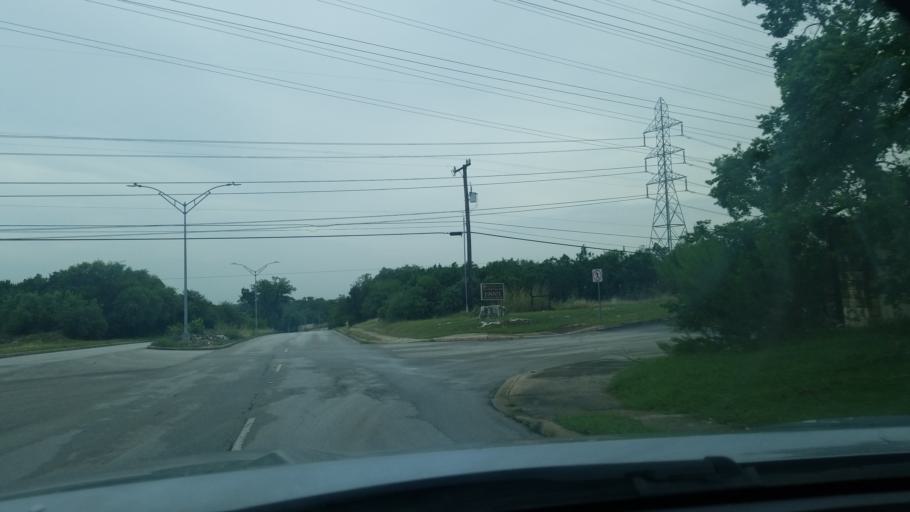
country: US
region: Texas
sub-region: Bexar County
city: Hollywood Park
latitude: 29.6186
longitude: -98.5164
